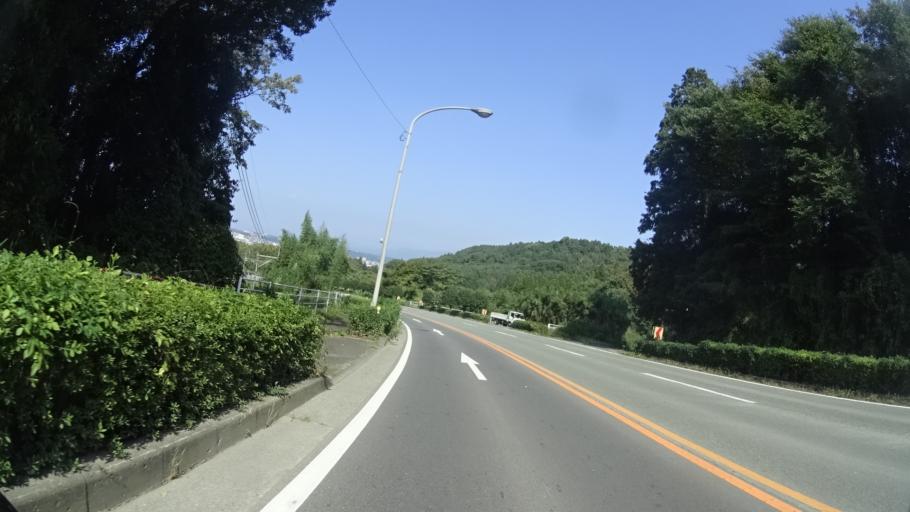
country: JP
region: Kumamoto
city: Ozu
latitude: 32.8475
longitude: 130.8608
